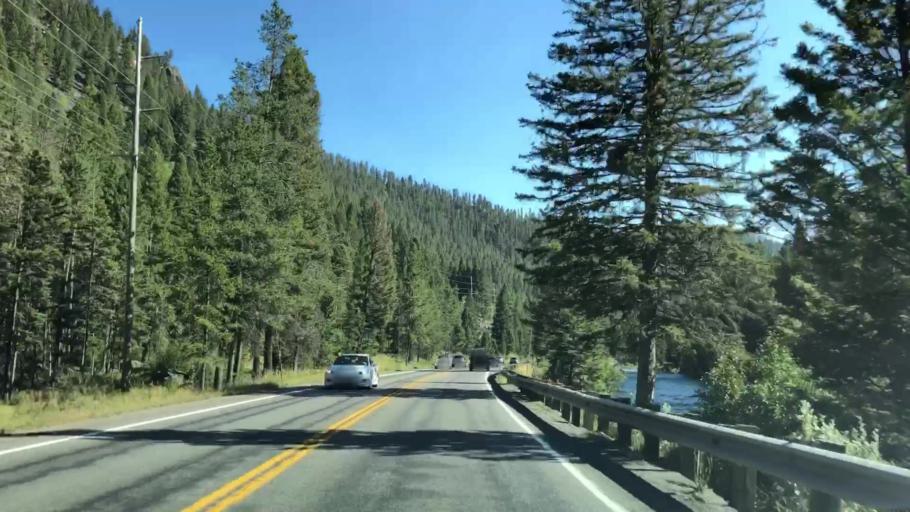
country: US
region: Montana
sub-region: Gallatin County
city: Big Sky
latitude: 45.3626
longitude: -111.1722
